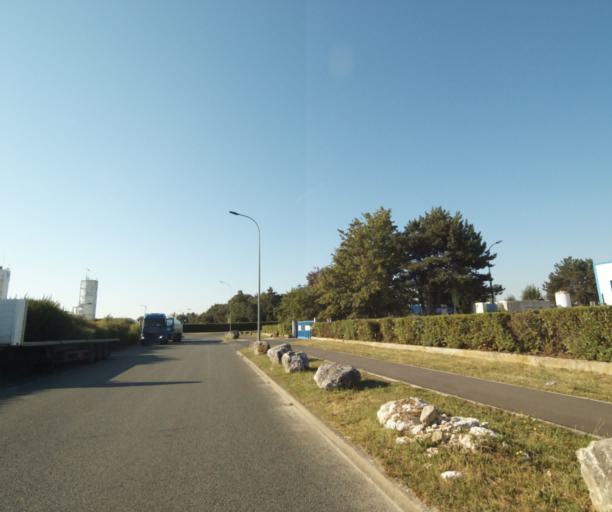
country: FR
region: Ile-de-France
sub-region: Departement de Seine-et-Marne
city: Moissy-Cramayel
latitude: 48.6161
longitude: 2.5724
